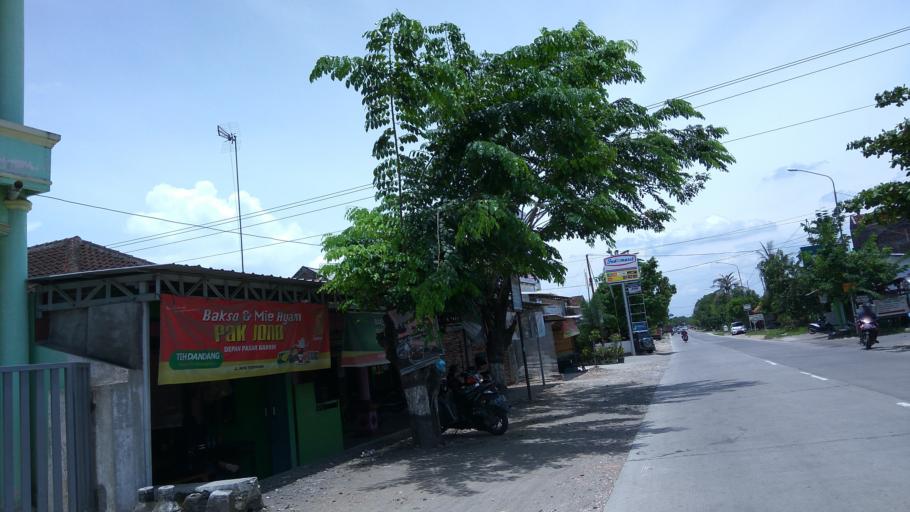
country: ID
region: Central Java
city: Mranggen
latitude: -7.0496
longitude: 110.5990
